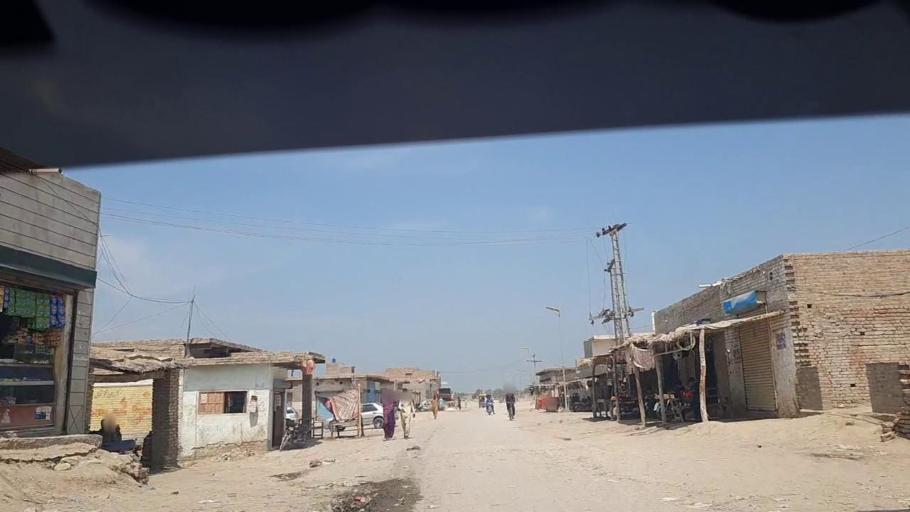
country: PK
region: Sindh
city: Thul
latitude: 28.1818
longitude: 68.7258
